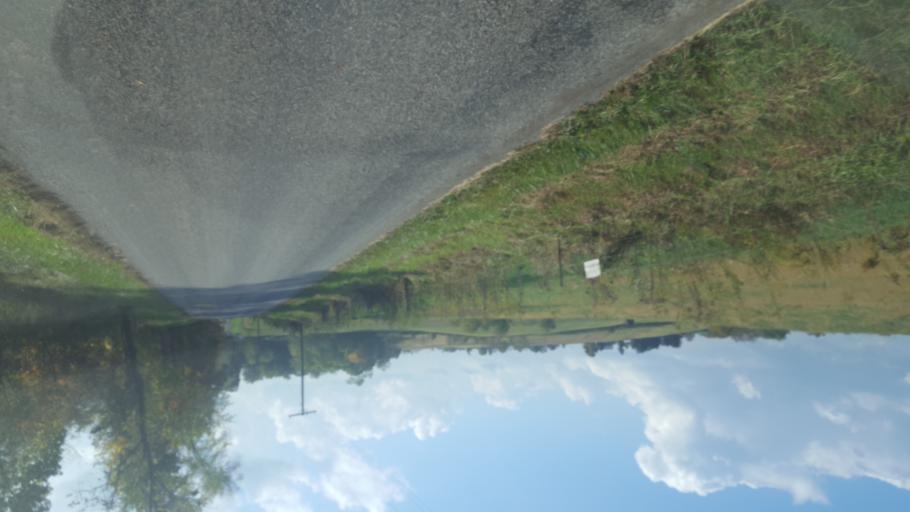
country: US
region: Ohio
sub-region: Holmes County
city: Millersburg
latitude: 40.6275
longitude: -81.8320
